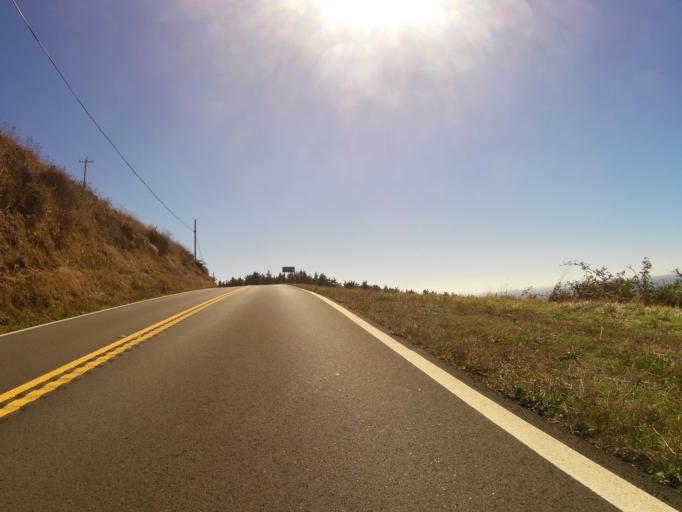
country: US
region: California
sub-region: Mendocino County
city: Fort Bragg
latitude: 39.6039
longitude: -123.7850
